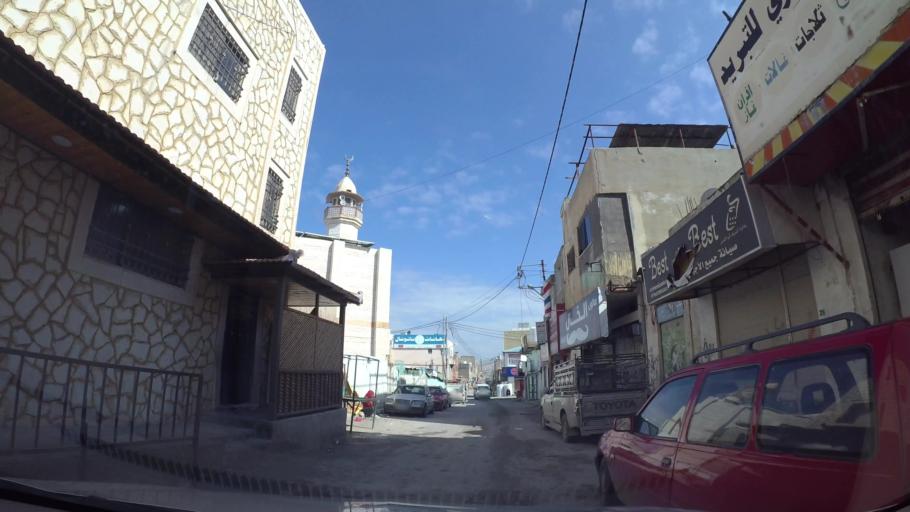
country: JO
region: Amman
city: Al Jubayhah
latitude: 32.0756
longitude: 35.8474
